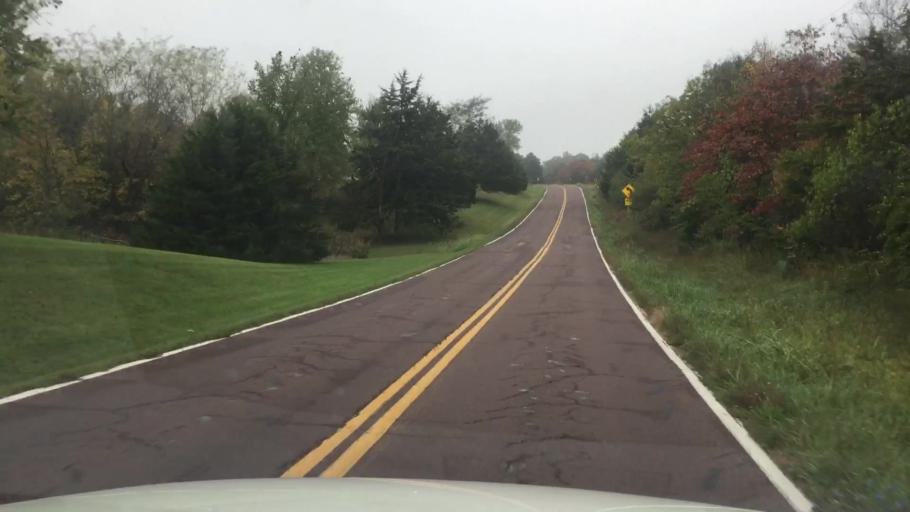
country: US
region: Missouri
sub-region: Boone County
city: Ashland
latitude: 38.8385
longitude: -92.3439
